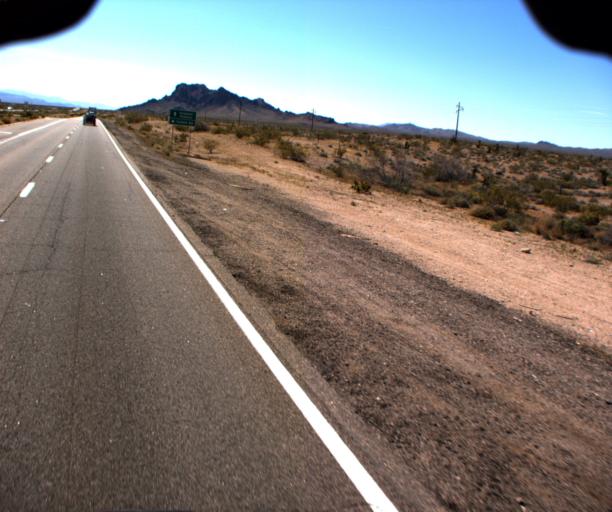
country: US
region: Nevada
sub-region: Clark County
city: Boulder City
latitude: 35.8209
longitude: -114.5535
